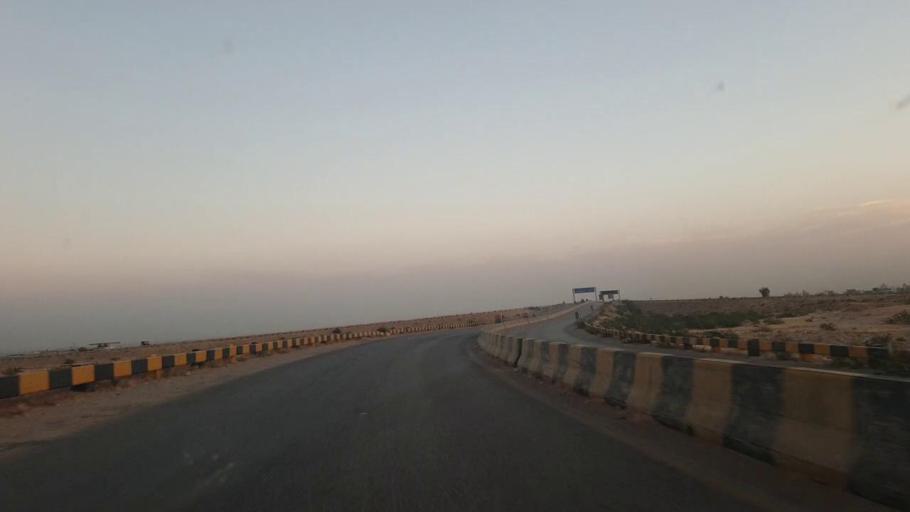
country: PK
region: Sindh
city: Jamshoro
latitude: 25.4035
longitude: 68.2716
